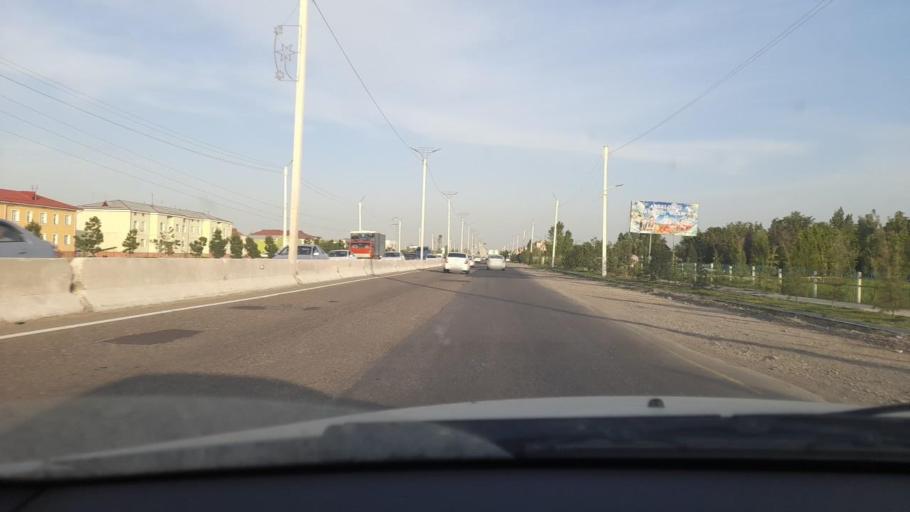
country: KZ
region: Ongtustik Qazaqstan
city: Myrzakent
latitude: 40.5492
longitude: 68.4043
